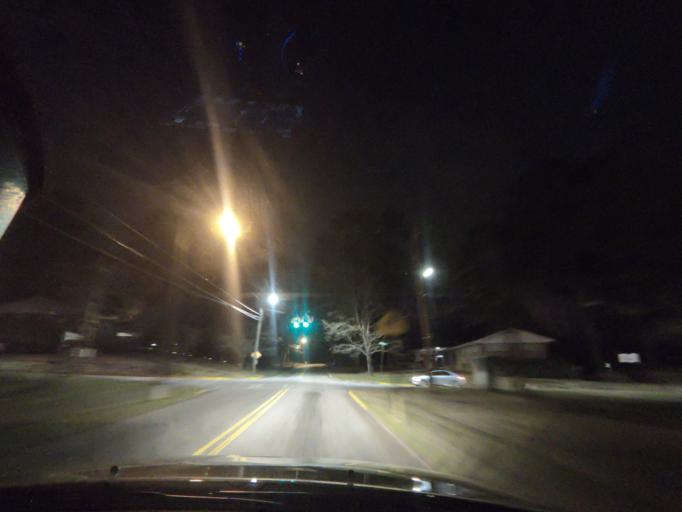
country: US
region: Georgia
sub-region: Fulton County
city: College Park
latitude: 33.6777
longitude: -84.4772
